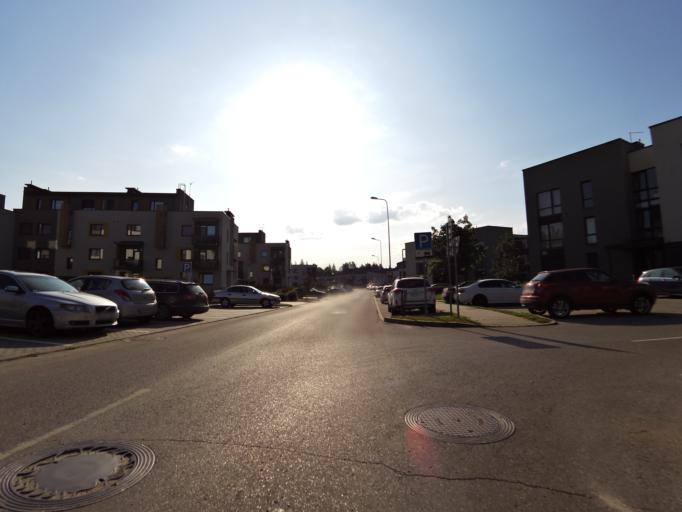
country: LT
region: Vilnius County
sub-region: Vilnius
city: Fabijoniskes
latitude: 54.7650
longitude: 25.2838
